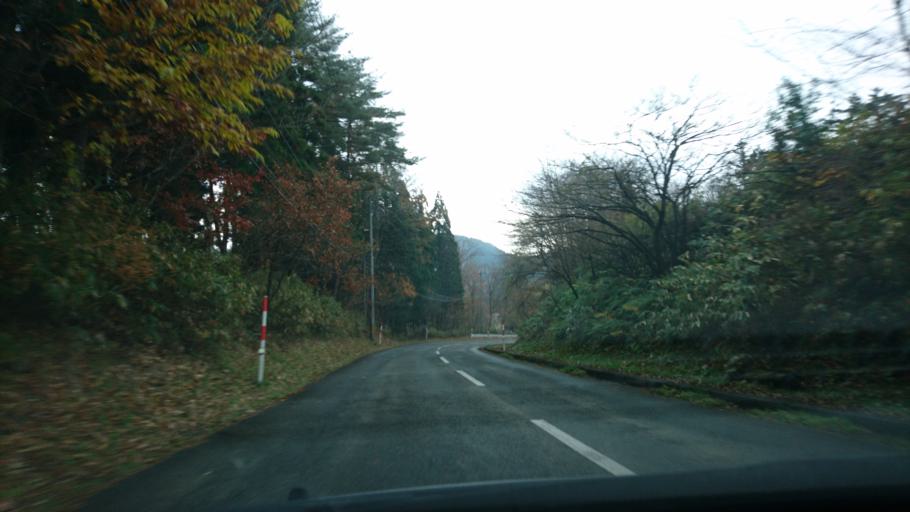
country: JP
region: Iwate
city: Ichinoseki
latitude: 38.9630
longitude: 140.9416
